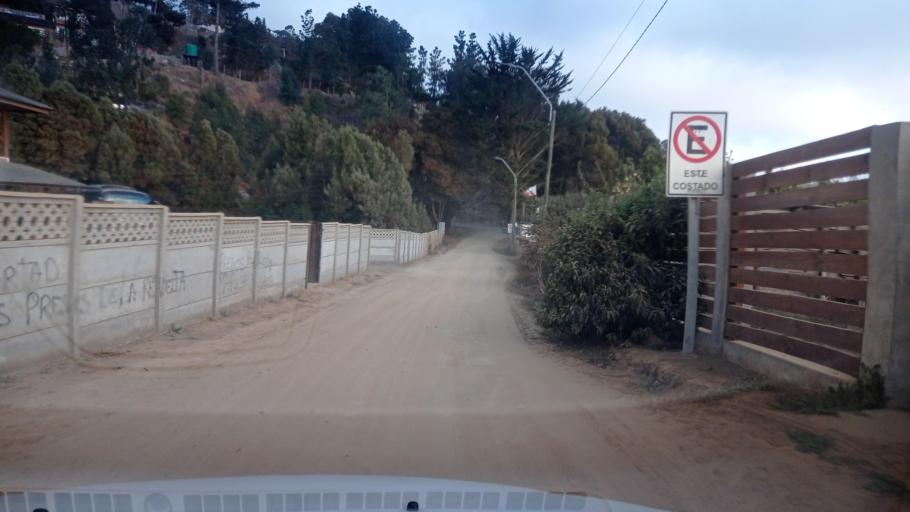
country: CL
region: O'Higgins
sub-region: Provincia de Colchagua
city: Santa Cruz
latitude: -34.4812
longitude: -72.0110
